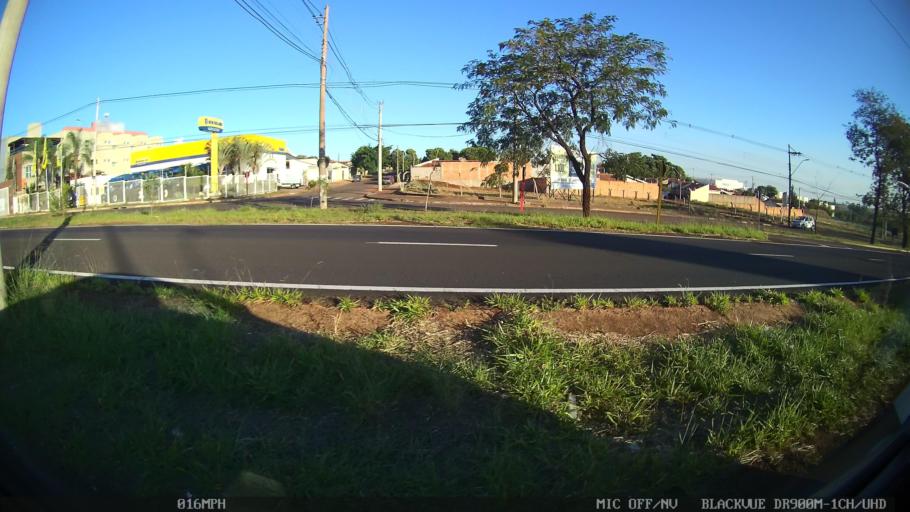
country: BR
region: Sao Paulo
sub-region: Araraquara
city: Araraquara
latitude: -21.7863
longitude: -48.2068
